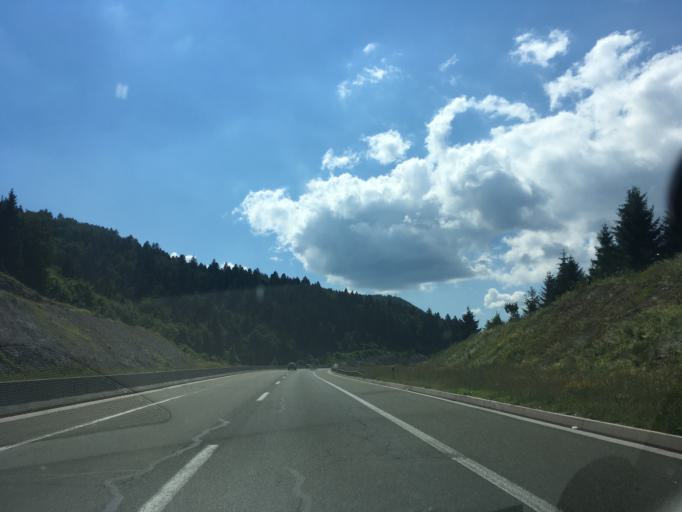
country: HR
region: Primorsko-Goranska
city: Vrbovsko
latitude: 45.3735
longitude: 14.9913
